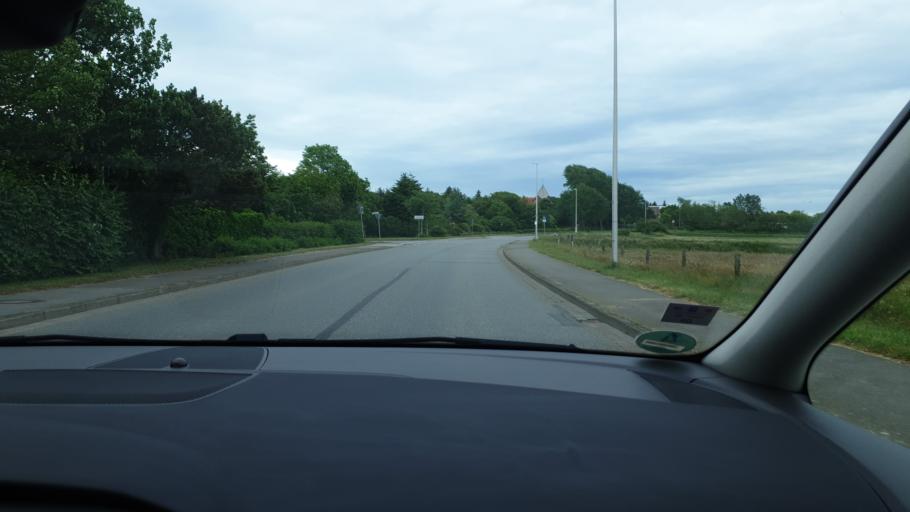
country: DE
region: Schleswig-Holstein
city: Schobull
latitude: 54.5119
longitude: 9.0008
